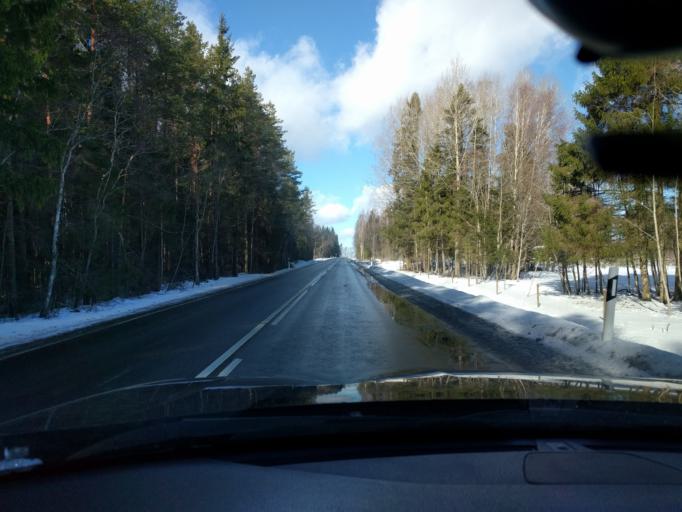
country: EE
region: Harju
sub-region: Raasiku vald
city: Raasiku
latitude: 59.2868
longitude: 25.1906
